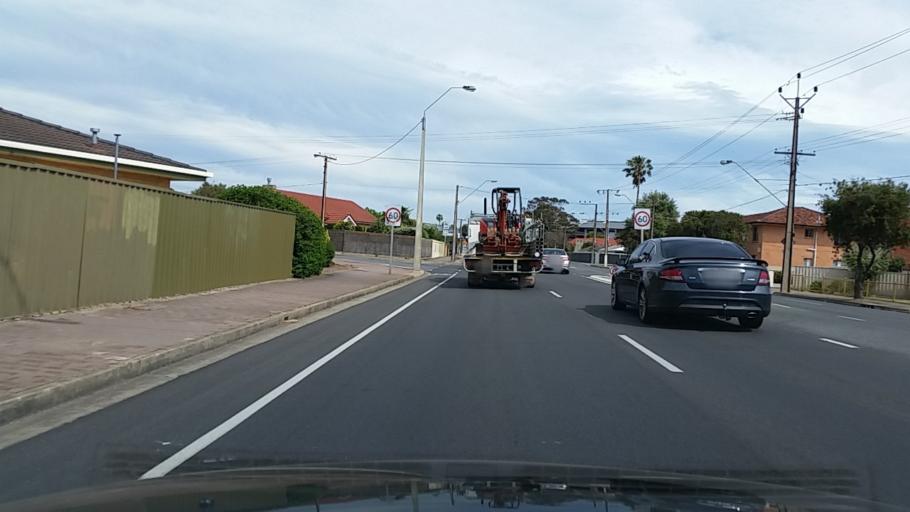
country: AU
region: South Australia
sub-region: Holdfast Bay
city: North Brighton
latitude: -34.9911
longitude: 138.5265
